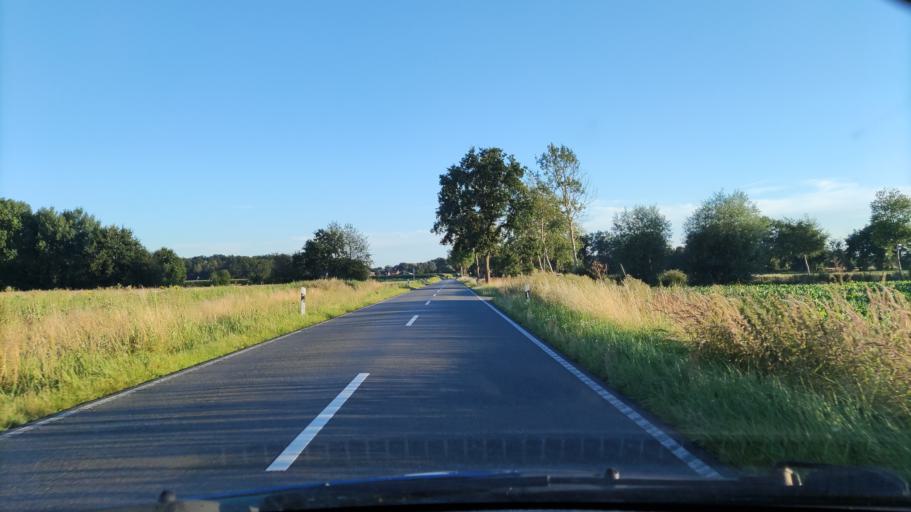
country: DE
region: Lower Saxony
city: Luechow
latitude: 53.0073
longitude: 11.1548
